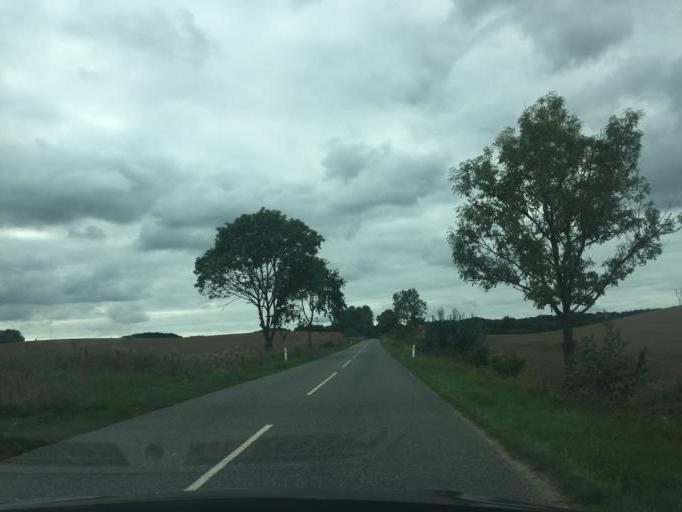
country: DK
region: South Denmark
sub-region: Assens Kommune
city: Tommerup
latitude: 55.3554
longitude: 10.2213
